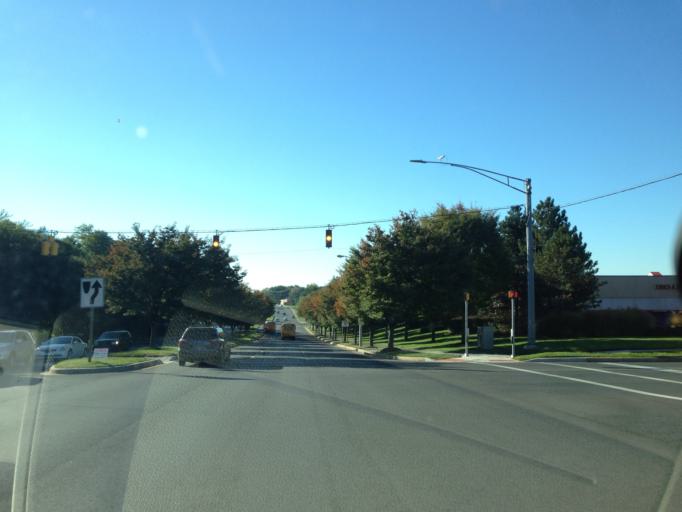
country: US
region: Maryland
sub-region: Montgomery County
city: Germantown
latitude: 39.2006
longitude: -77.2454
